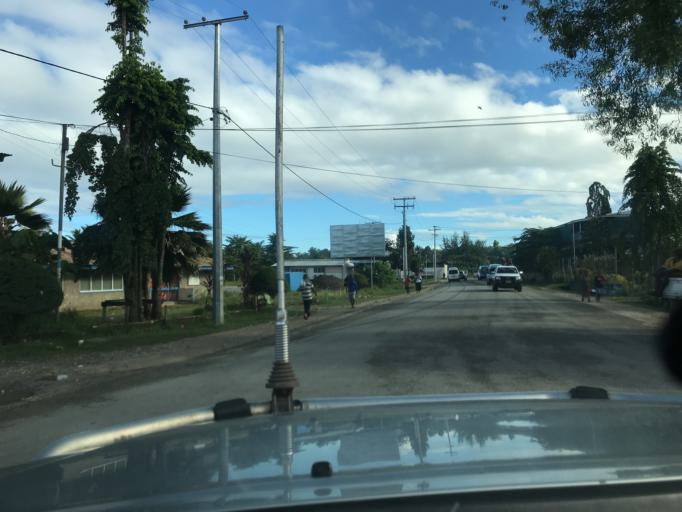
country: SB
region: Malaita
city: Auki
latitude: -8.7714
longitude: 160.6973
